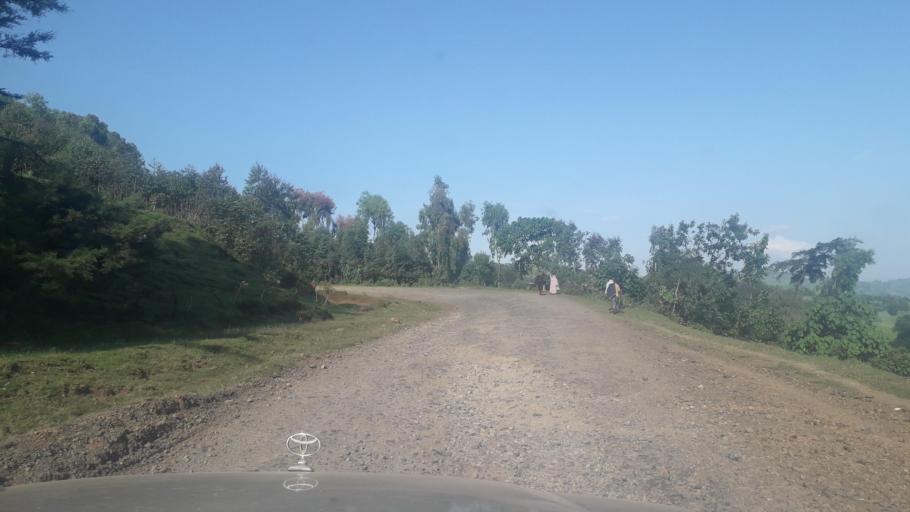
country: ET
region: Oromiya
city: Jima
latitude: 7.4273
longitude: 36.8720
